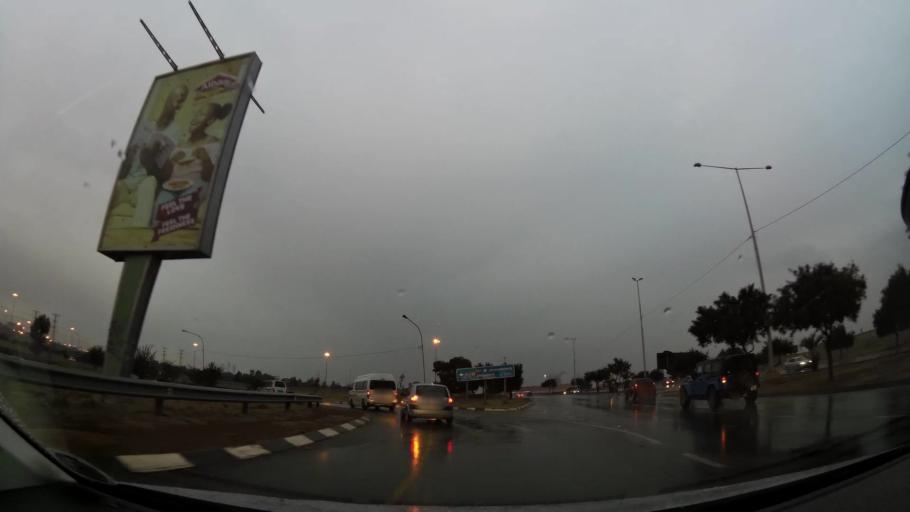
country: ZA
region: Gauteng
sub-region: City of Johannesburg Metropolitan Municipality
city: Soweto
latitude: -26.2621
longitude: 27.9548
